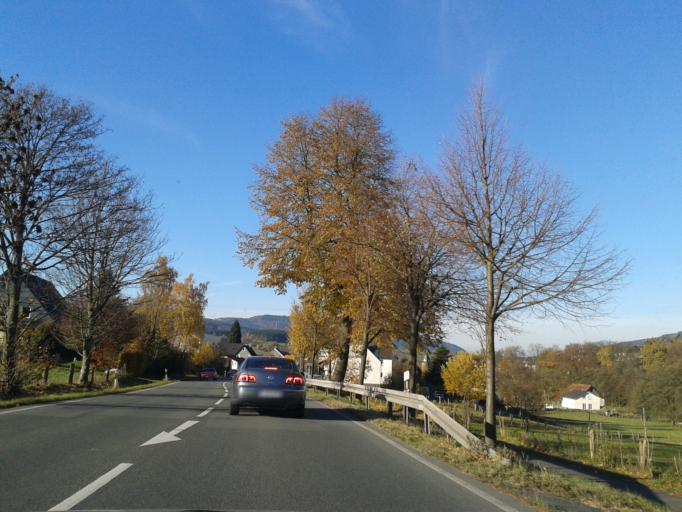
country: DE
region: North Rhine-Westphalia
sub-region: Regierungsbezirk Arnsberg
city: Olsberg
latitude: 51.2858
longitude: 8.5063
